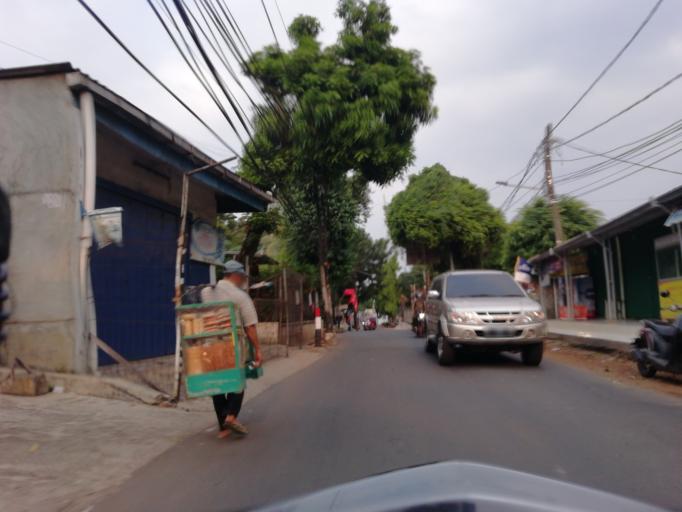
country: ID
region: West Java
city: Depok
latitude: -6.3271
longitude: 106.8112
